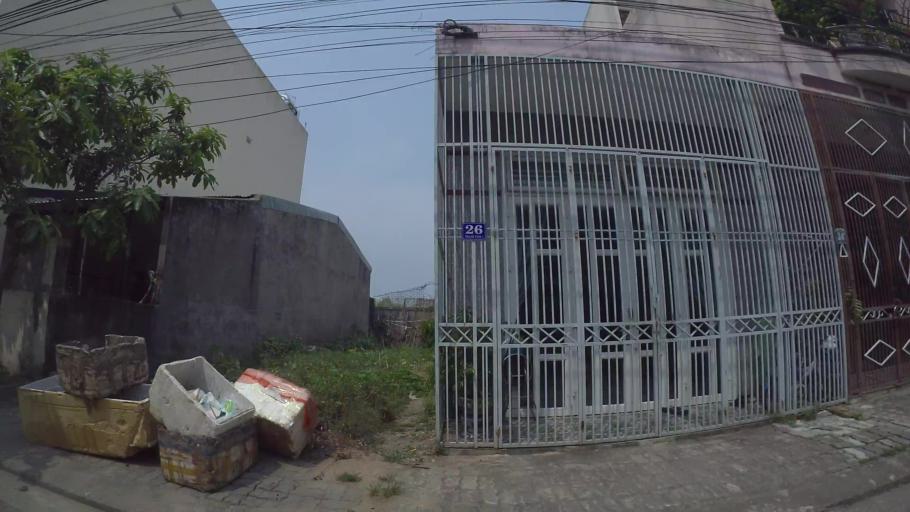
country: VN
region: Da Nang
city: Da Nang
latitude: 16.1062
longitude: 108.2518
